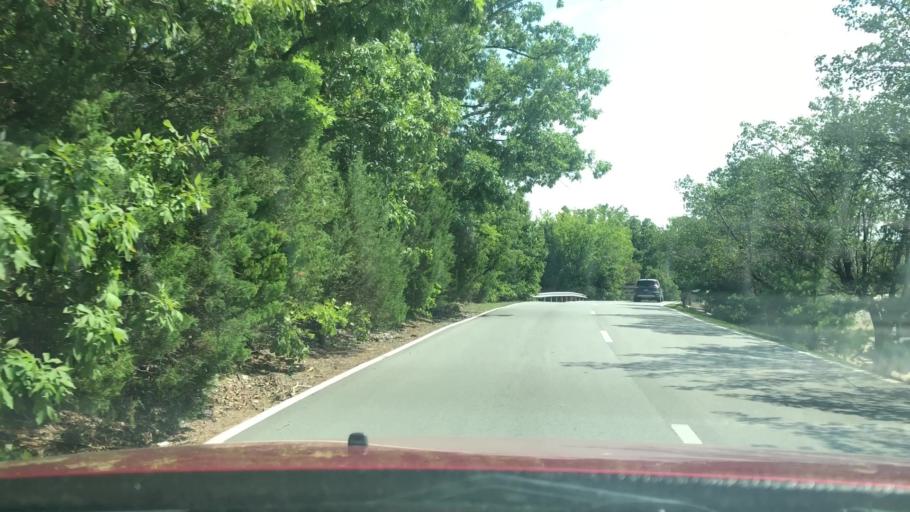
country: US
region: Missouri
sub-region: Stone County
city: Kimberling City
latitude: 36.6635
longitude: -93.3378
